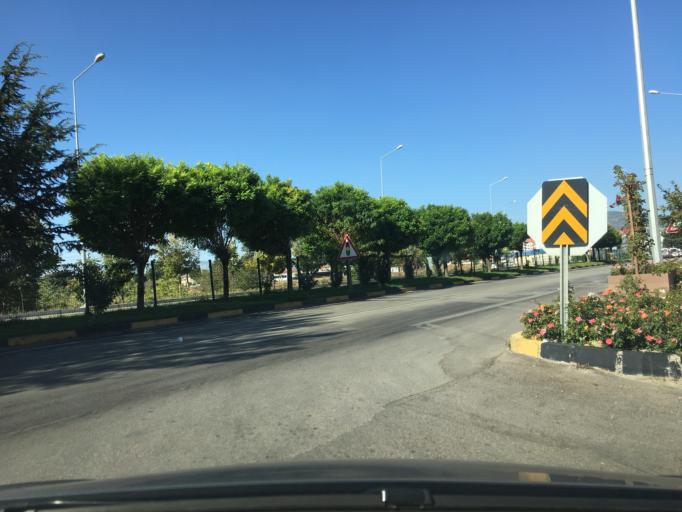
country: TR
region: Isparta
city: Isparta
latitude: 37.7911
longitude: 30.5458
